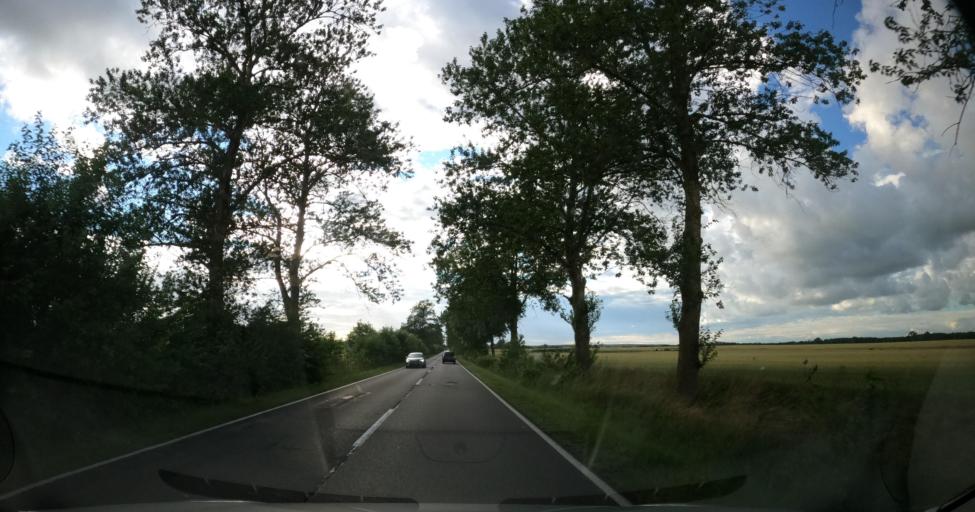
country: PL
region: Pomeranian Voivodeship
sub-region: Powiat slupski
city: Damnica
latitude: 54.4253
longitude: 17.3728
